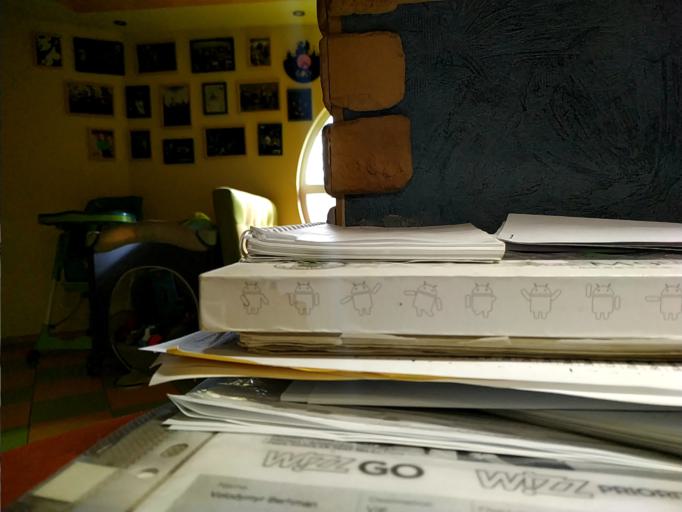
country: RU
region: Novgorod
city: Volot
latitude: 57.6523
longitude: 30.7340
